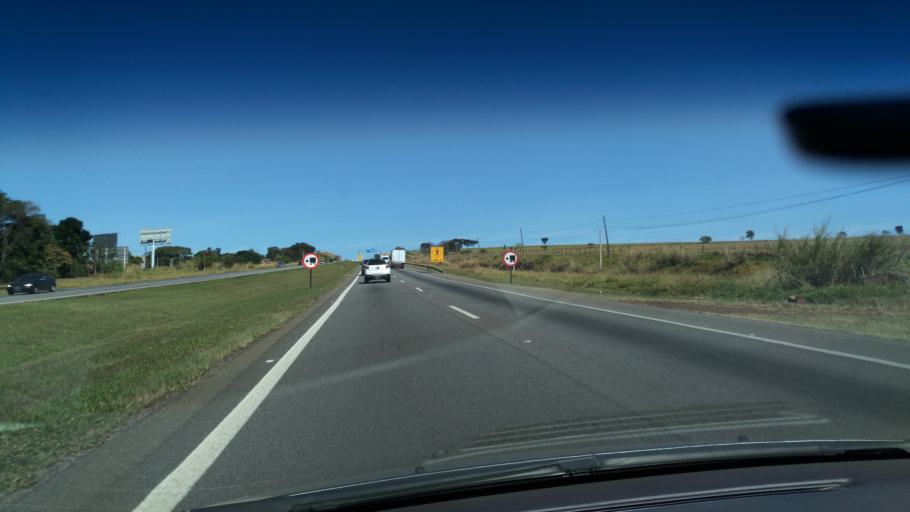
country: BR
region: Sao Paulo
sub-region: Jaguariuna
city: Jaguariuna
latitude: -22.7520
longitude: -47.0206
